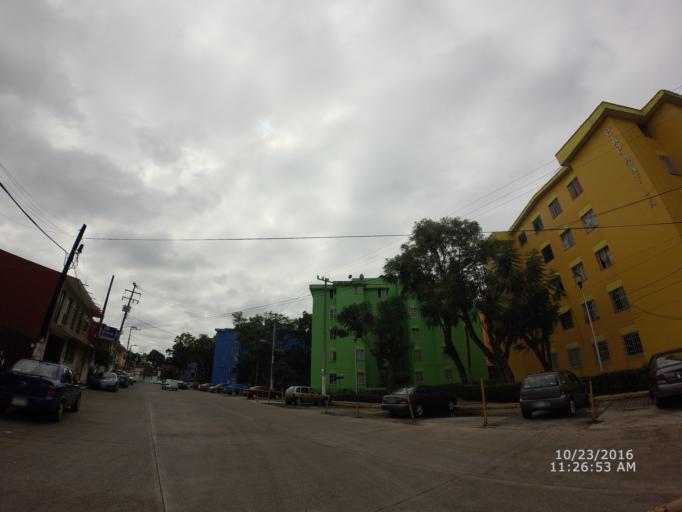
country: MX
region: Veracruz
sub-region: Tlalnelhuayocan
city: Guadalupe Victoria
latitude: 19.5494
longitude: -96.9412
